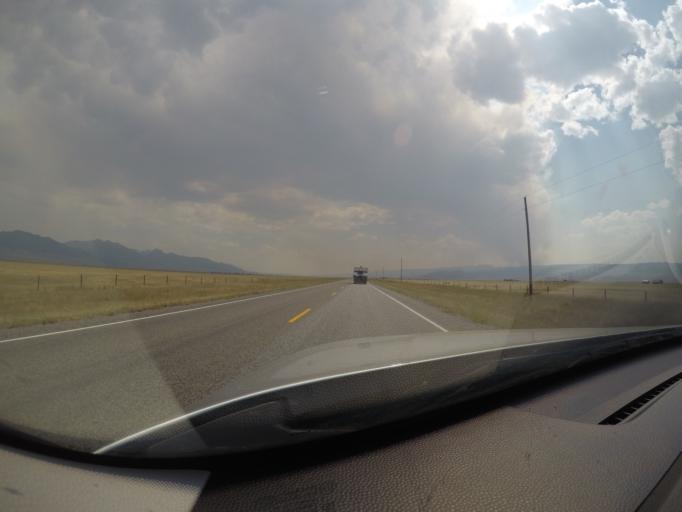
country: US
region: Montana
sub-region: Madison County
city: Virginia City
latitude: 45.1806
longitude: -111.6789
